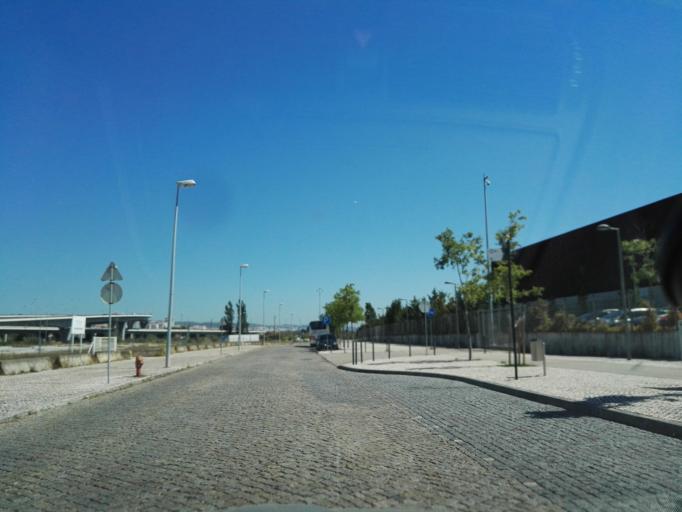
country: PT
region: Lisbon
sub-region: Loures
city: Sacavem
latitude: 38.7938
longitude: -9.0976
